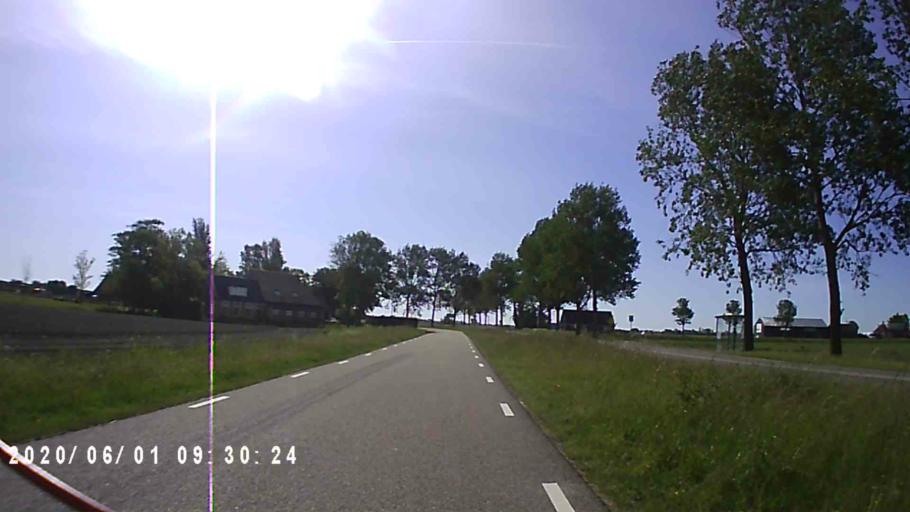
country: NL
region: Friesland
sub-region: Gemeente Leeuwarderadeel
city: Stiens
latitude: 53.2657
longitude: 5.7341
